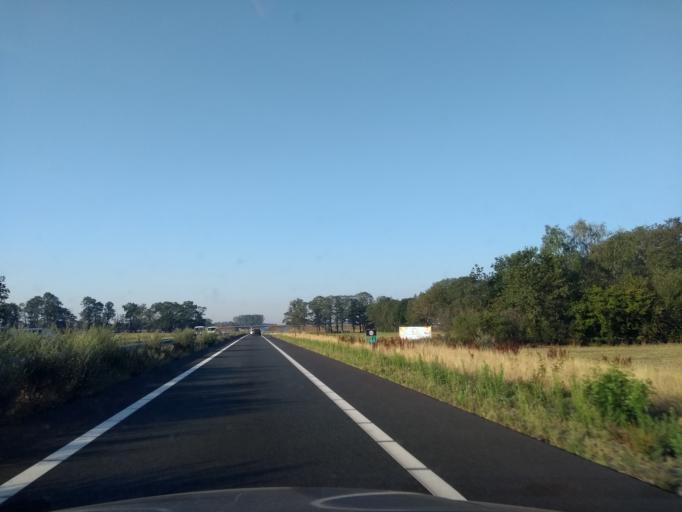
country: NL
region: Gelderland
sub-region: Berkelland
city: Eibergen
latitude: 52.0690
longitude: 6.6340
